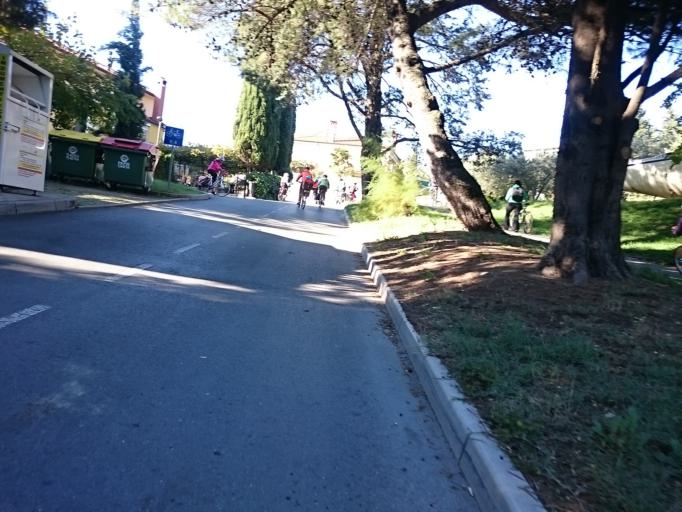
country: SI
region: Piran-Pirano
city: Lucija
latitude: 45.5076
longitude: 13.6011
